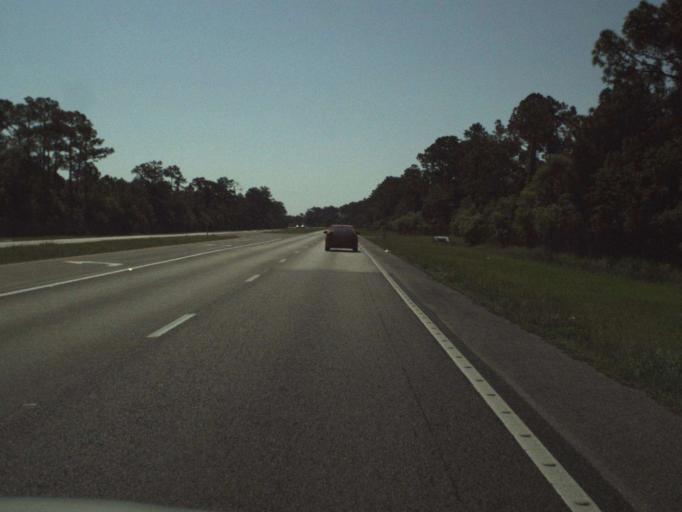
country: US
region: Florida
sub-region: Brevard County
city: Cocoa West
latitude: 28.3749
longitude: -80.9056
